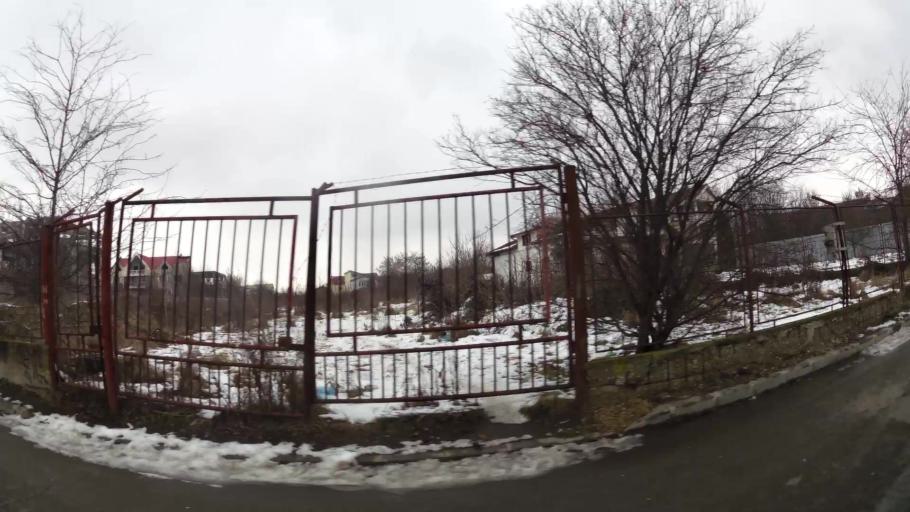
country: RO
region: Ilfov
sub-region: Comuna Otopeni
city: Otopeni
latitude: 44.5432
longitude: 26.0714
